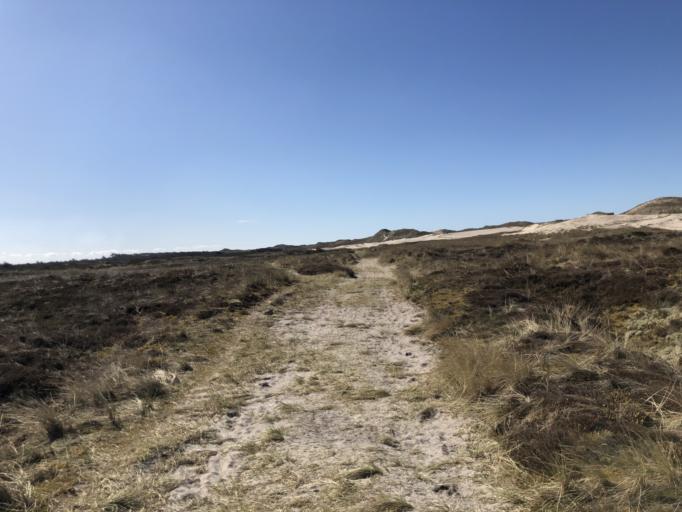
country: DK
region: Central Jutland
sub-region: Holstebro Kommune
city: Ulfborg
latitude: 56.3134
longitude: 8.1277
